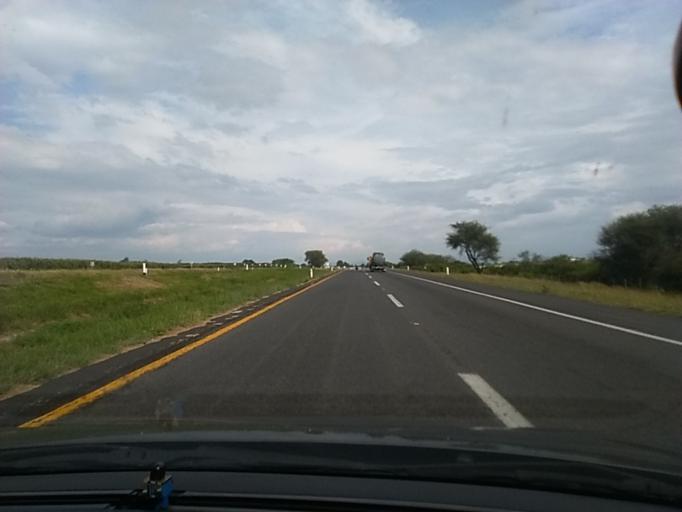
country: MX
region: Jalisco
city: La Barca
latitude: 20.3419
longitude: -102.6125
